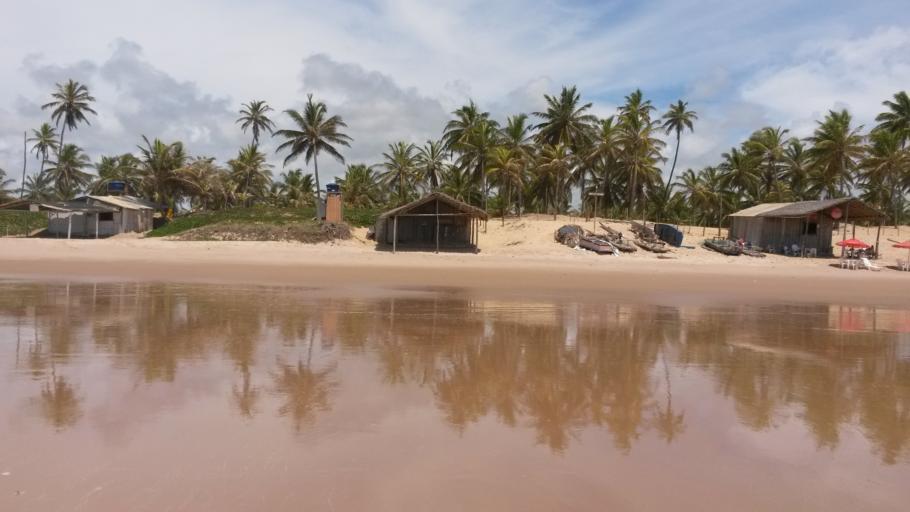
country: BR
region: Bahia
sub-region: Mata De Sao Joao
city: Mata de Sao Joao
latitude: -12.4613
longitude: -37.9326
